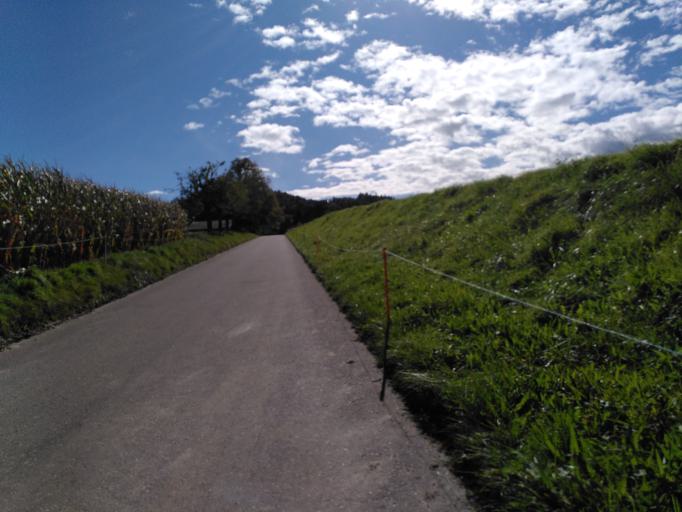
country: CH
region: Bern
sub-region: Oberaargau
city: Seeberg
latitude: 47.1360
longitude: 7.7159
